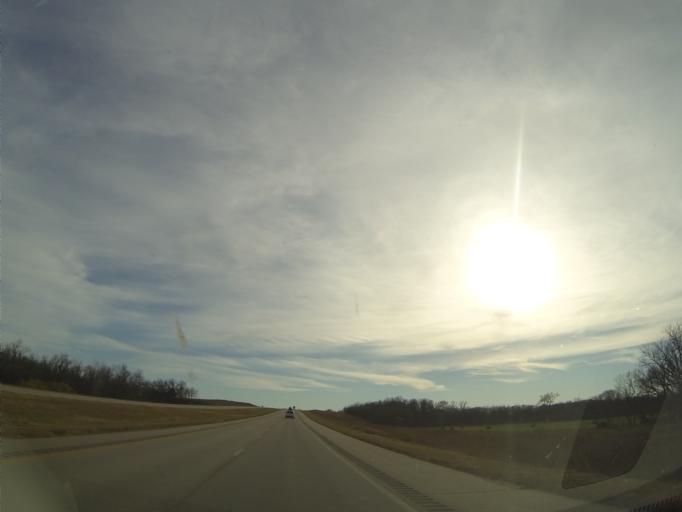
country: US
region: Kansas
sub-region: Ottawa County
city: Minneapolis
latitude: 39.1885
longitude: -97.6677
